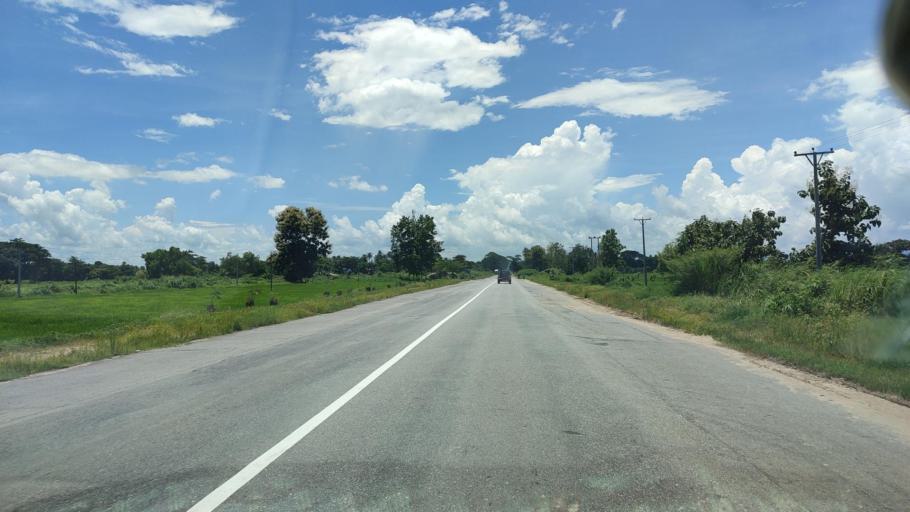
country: MM
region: Bago
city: Taungoo
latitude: 18.7283
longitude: 96.4076
